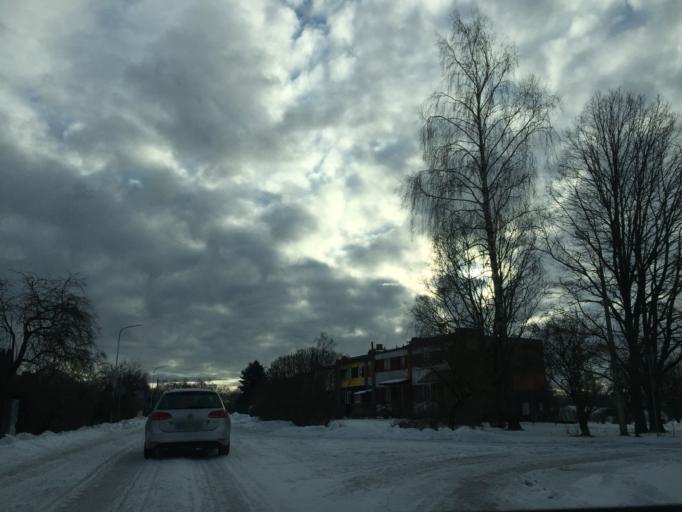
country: LV
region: Lielvarde
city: Lielvarde
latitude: 56.6346
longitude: 24.7522
